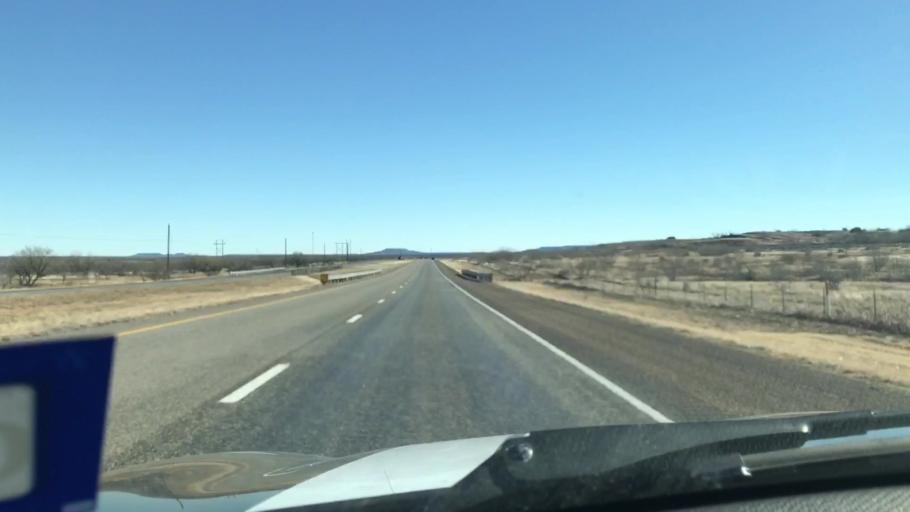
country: US
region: Texas
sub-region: Garza County
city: Post
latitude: 33.0641
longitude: -101.2226
